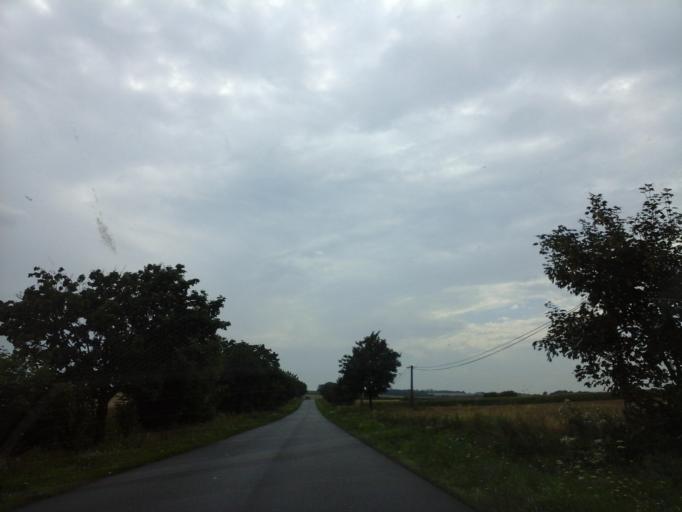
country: PL
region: Lower Silesian Voivodeship
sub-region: Powiat zabkowicki
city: Cieplowody
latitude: 50.6619
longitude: 16.9070
